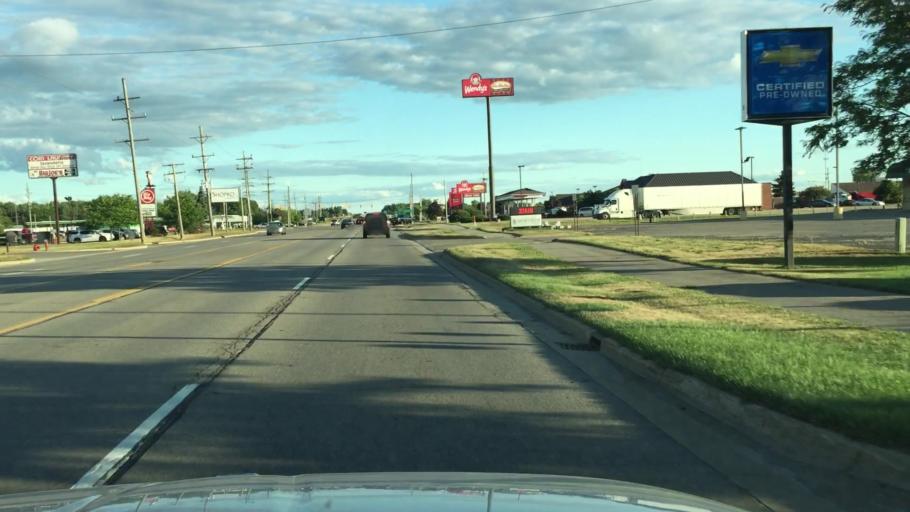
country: US
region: Michigan
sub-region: Lapeer County
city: Imlay City
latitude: 43.0094
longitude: -83.0717
